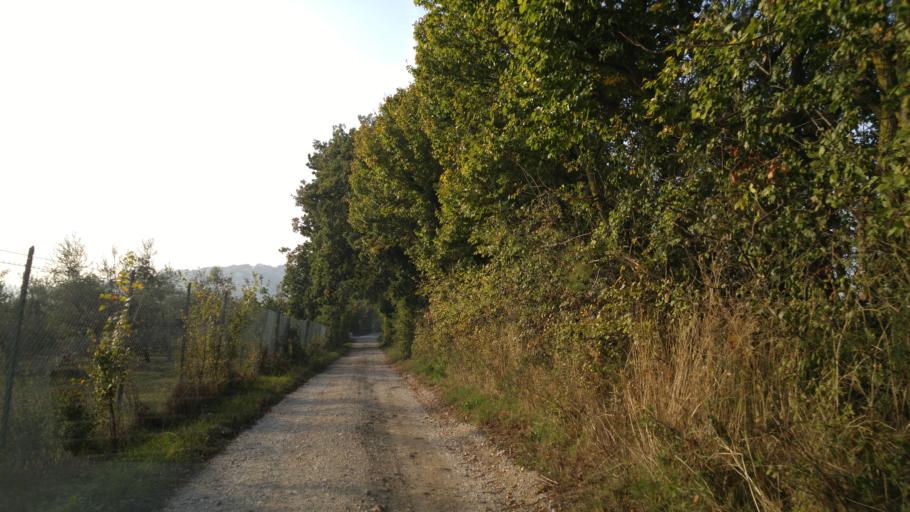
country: IT
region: The Marches
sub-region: Provincia di Pesaro e Urbino
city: Fenile
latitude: 43.8718
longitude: 12.9657
